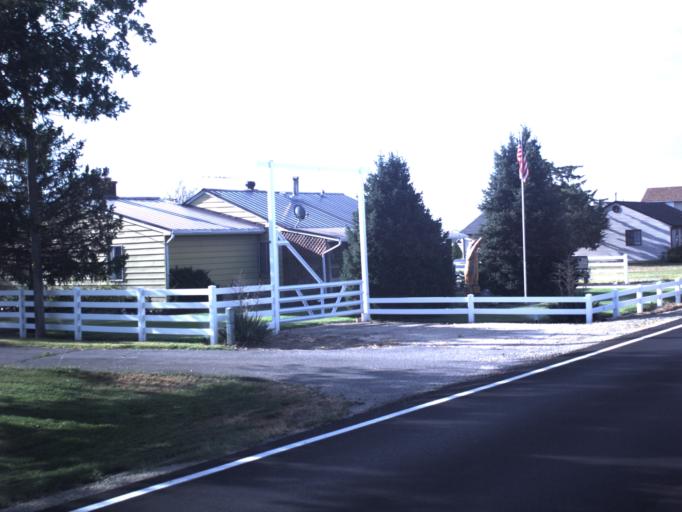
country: US
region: Utah
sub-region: Weber County
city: West Haven
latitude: 41.2318
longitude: -112.0928
